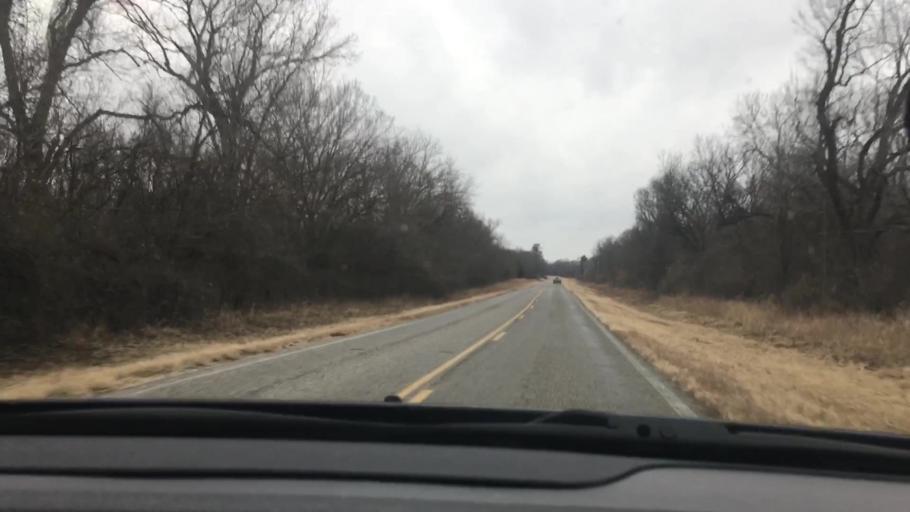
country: US
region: Oklahoma
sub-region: Johnston County
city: Tishomingo
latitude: 34.2167
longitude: -96.6361
